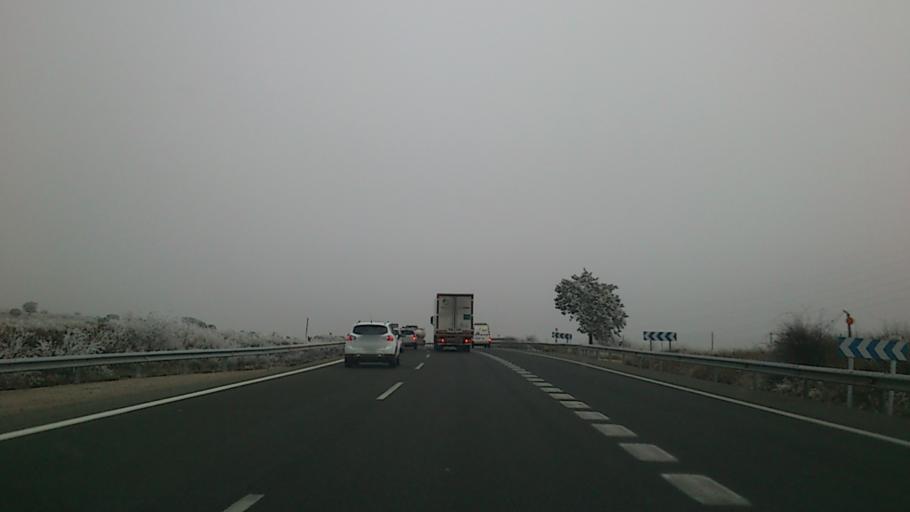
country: ES
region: Castille-La Mancha
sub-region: Provincia de Guadalajara
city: Torremocha del Campo
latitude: 40.9906
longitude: -2.5935
